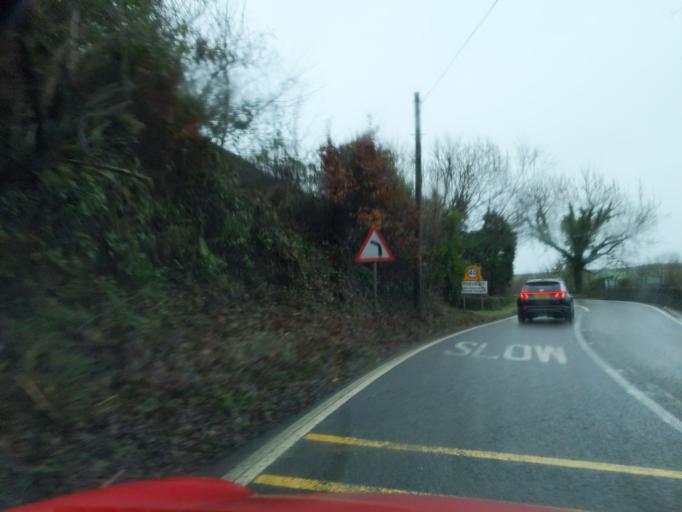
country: GB
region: England
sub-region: Cornwall
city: South Hill
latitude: 50.5721
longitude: -4.3321
